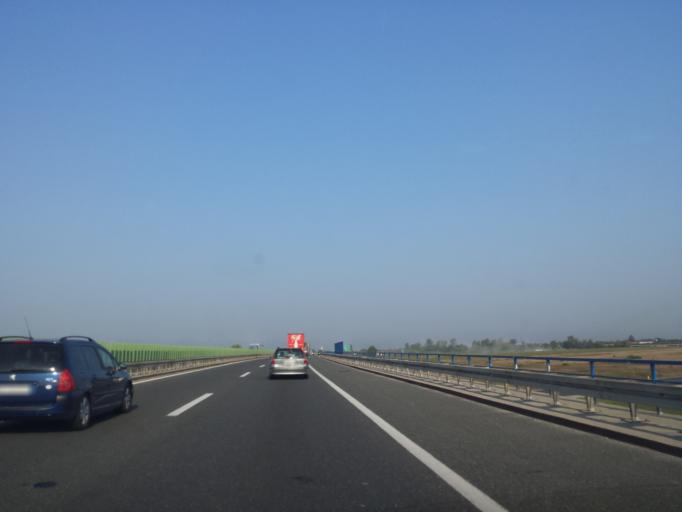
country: HR
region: Grad Zagreb
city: Zadvorsko
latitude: 45.7486
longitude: 15.9211
